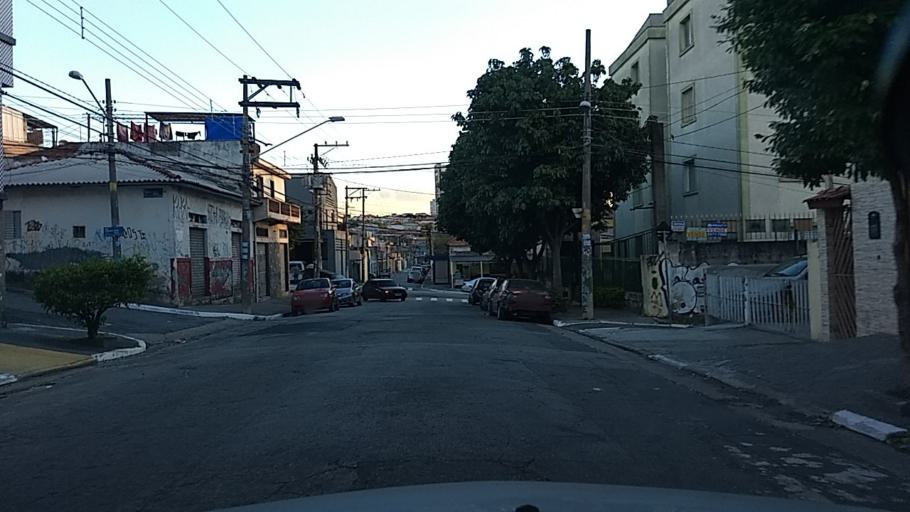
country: BR
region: Sao Paulo
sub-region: Guarulhos
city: Guarulhos
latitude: -23.4890
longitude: -46.5872
